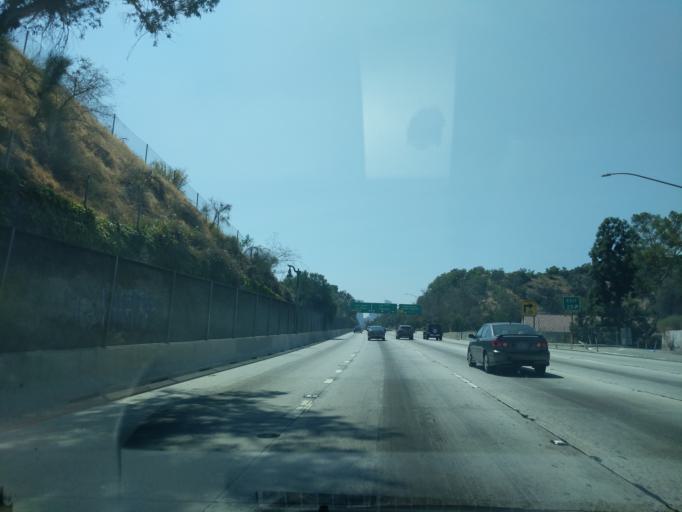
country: US
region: California
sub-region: Los Angeles County
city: Los Angeles
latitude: 34.0766
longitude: -118.2309
